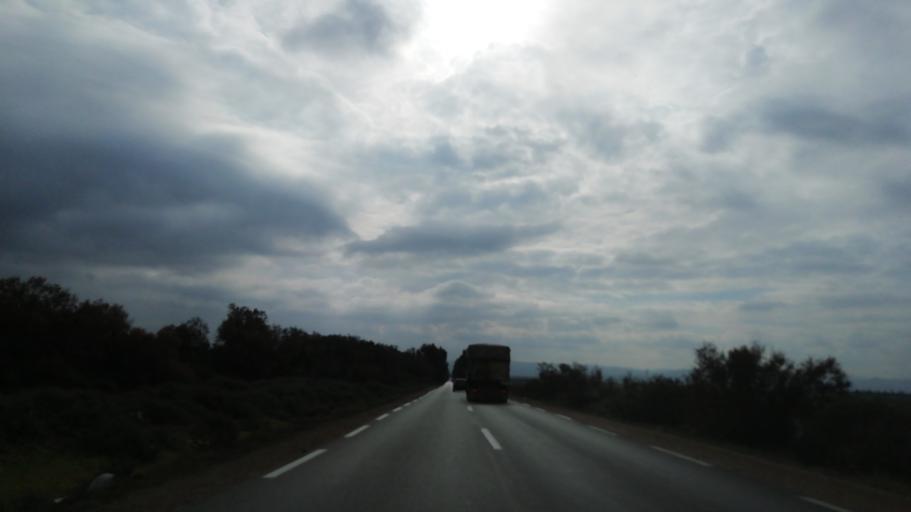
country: DZ
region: Oran
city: Sidi ech Chahmi
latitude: 35.5859
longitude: -0.4532
